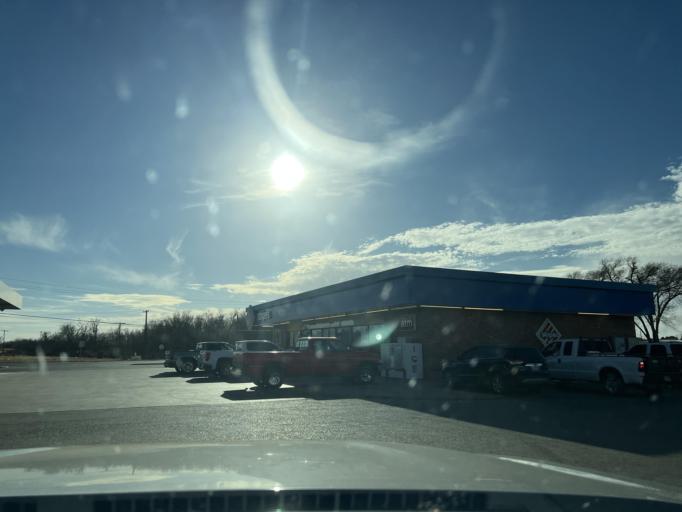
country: US
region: Texas
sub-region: Scurry County
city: Snyder
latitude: 32.7051
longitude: -100.8841
